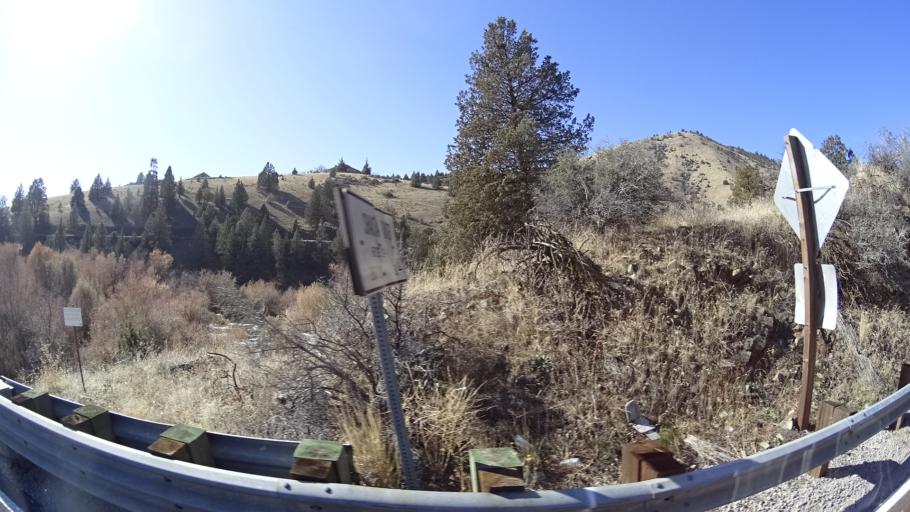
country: US
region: California
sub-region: Siskiyou County
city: Yreka
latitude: 41.7820
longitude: -122.5968
